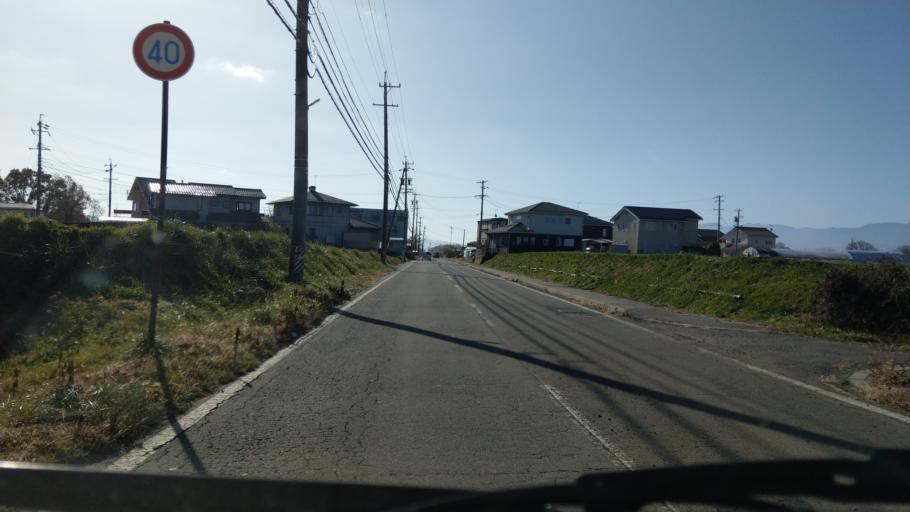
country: JP
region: Nagano
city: Komoro
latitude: 36.3004
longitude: 138.4852
